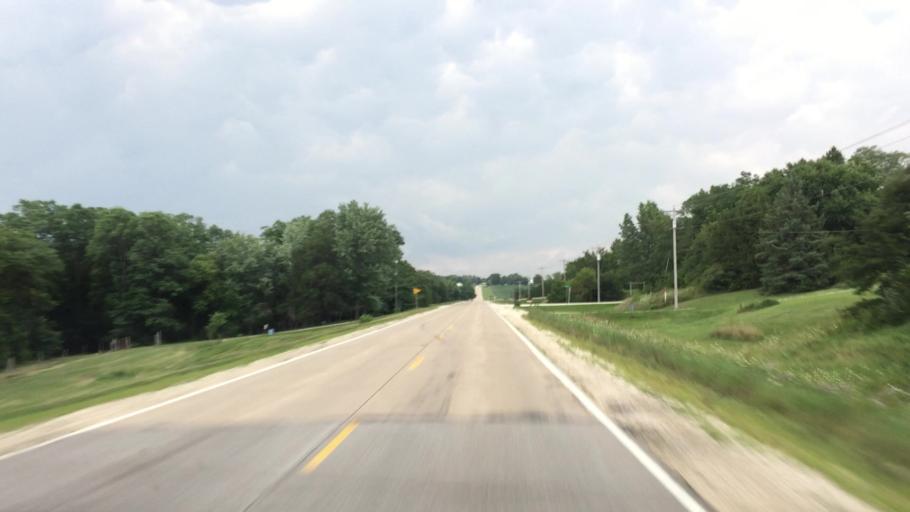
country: US
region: Iowa
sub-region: Lee County
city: Fort Madison
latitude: 40.7171
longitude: -91.3299
